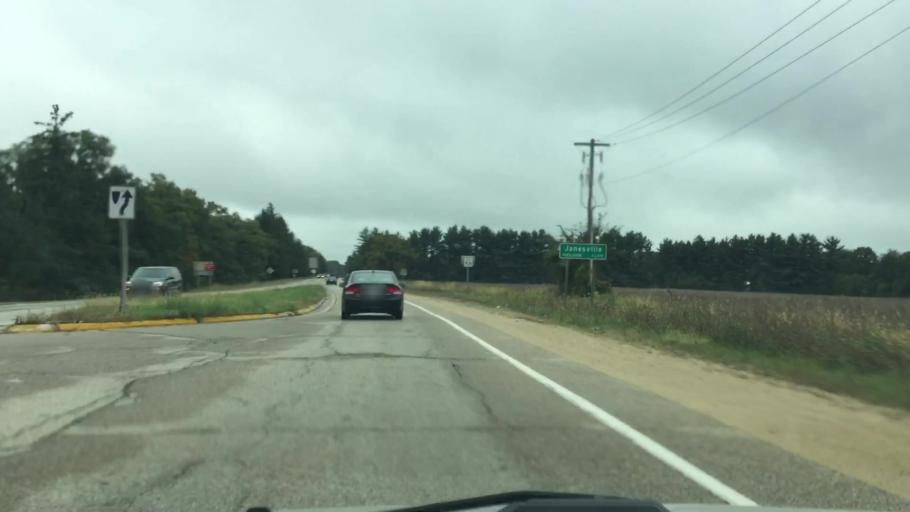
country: US
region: Wisconsin
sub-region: Rock County
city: Janesville
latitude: 42.7279
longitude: -89.0331
